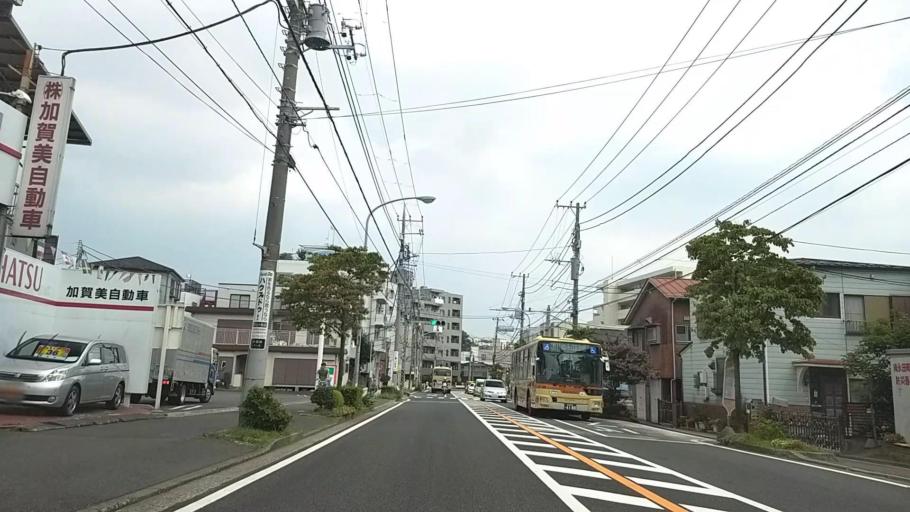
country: JP
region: Kanagawa
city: Yokohama
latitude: 35.4289
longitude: 139.5968
